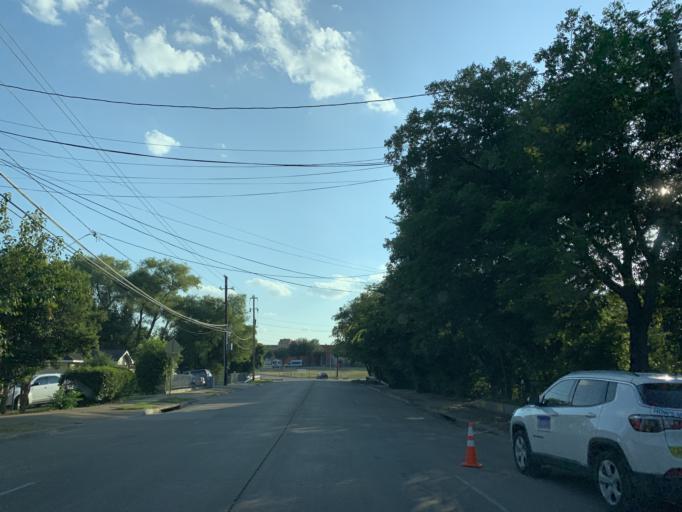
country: US
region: Texas
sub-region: Dallas County
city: Hutchins
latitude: 32.6979
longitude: -96.7853
